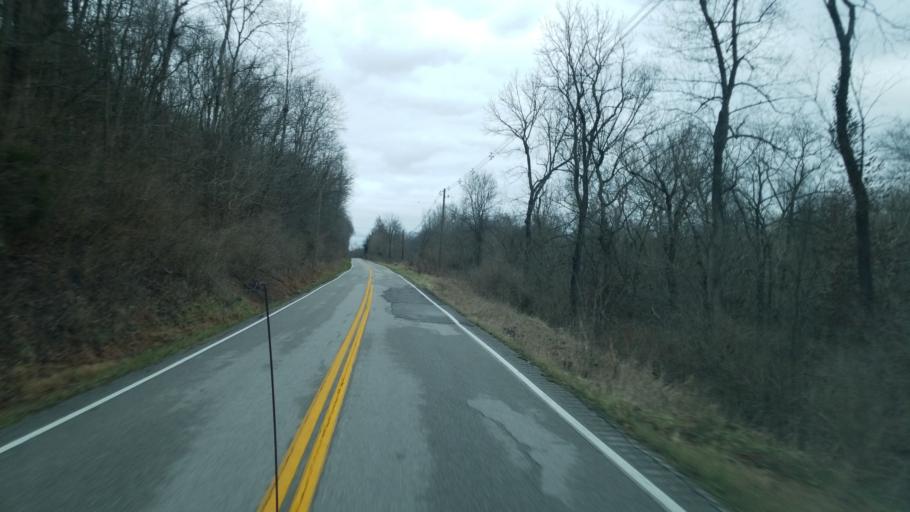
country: US
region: Ohio
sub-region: Clermont County
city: New Richmond
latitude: 38.9083
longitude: -84.2614
